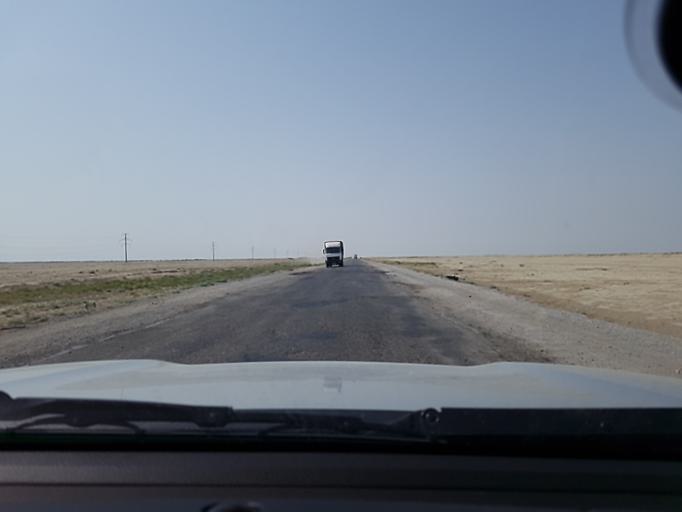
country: TM
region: Balkan
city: Gumdag
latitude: 38.8707
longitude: 54.5943
